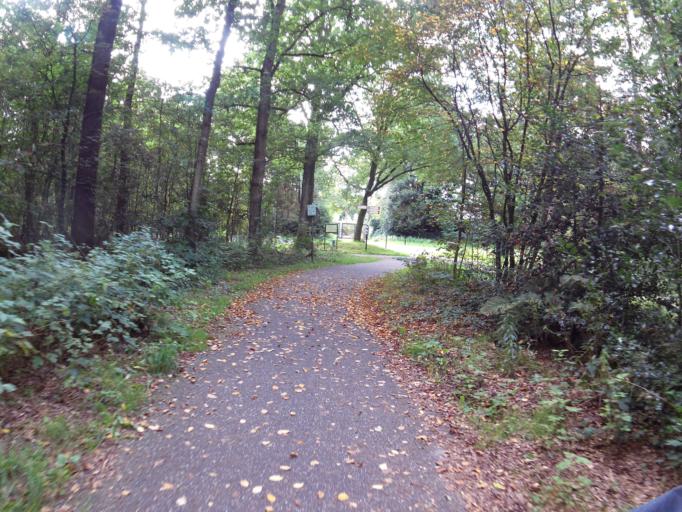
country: NL
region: Drenthe
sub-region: Gemeente Borger-Odoorn
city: Borger
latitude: 52.9337
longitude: 6.7512
